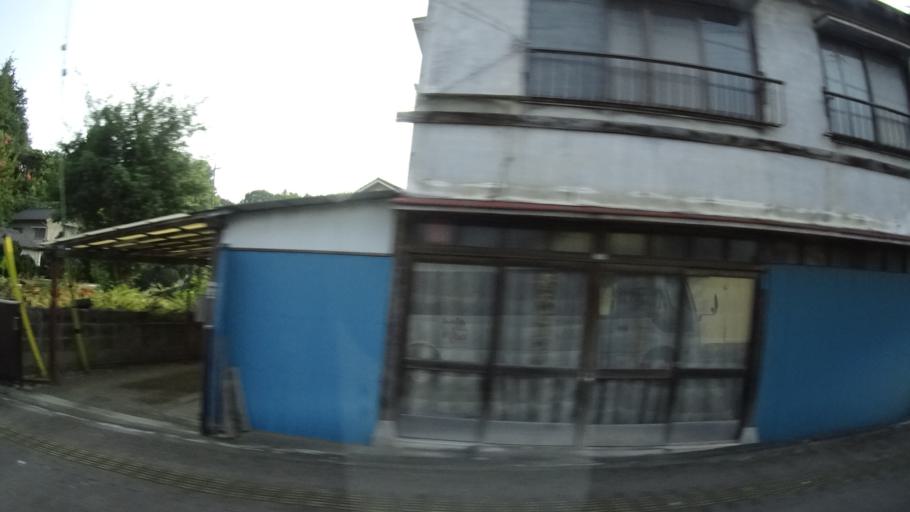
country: JP
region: Tochigi
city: Karasuyama
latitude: 36.6482
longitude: 140.1520
